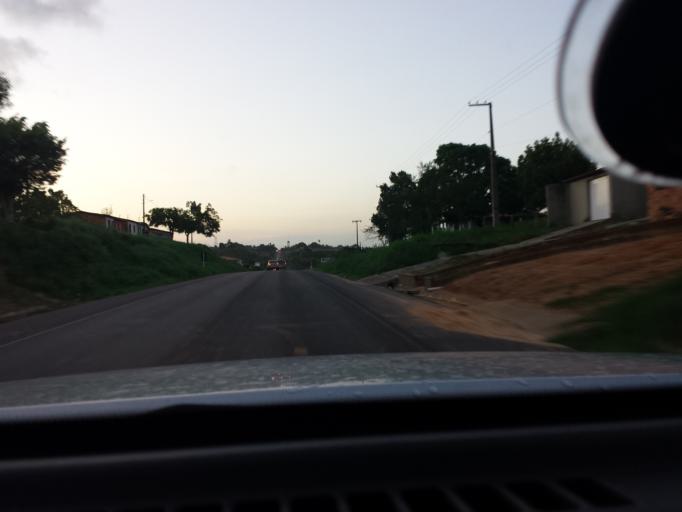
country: BR
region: Sergipe
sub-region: Salgado
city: Salgado
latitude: -10.9999
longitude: -37.5214
